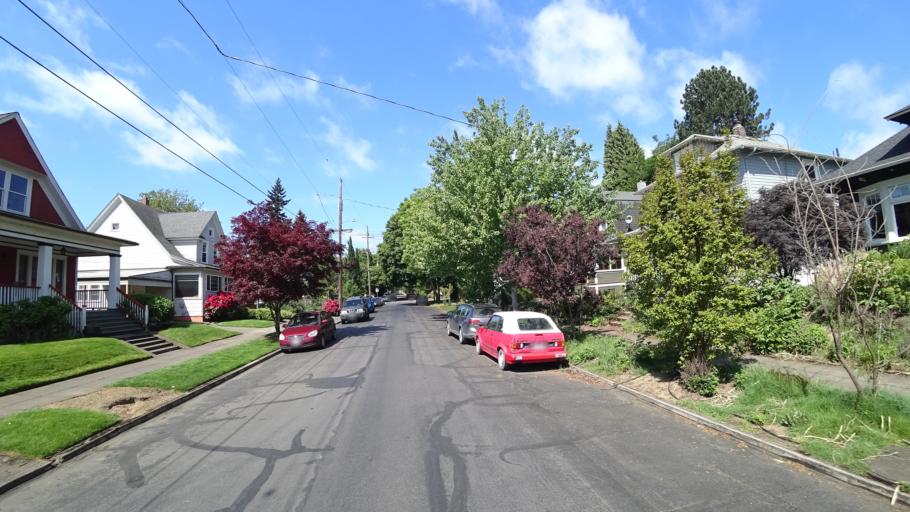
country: US
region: Oregon
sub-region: Multnomah County
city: Portland
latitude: 45.5136
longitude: -122.6339
